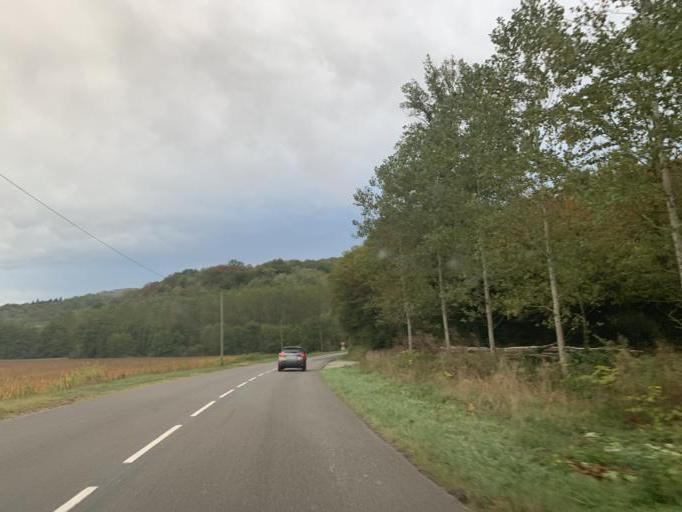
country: FR
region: Rhone-Alpes
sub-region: Departement de l'Ain
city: Belley
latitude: 45.7157
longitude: 5.6643
